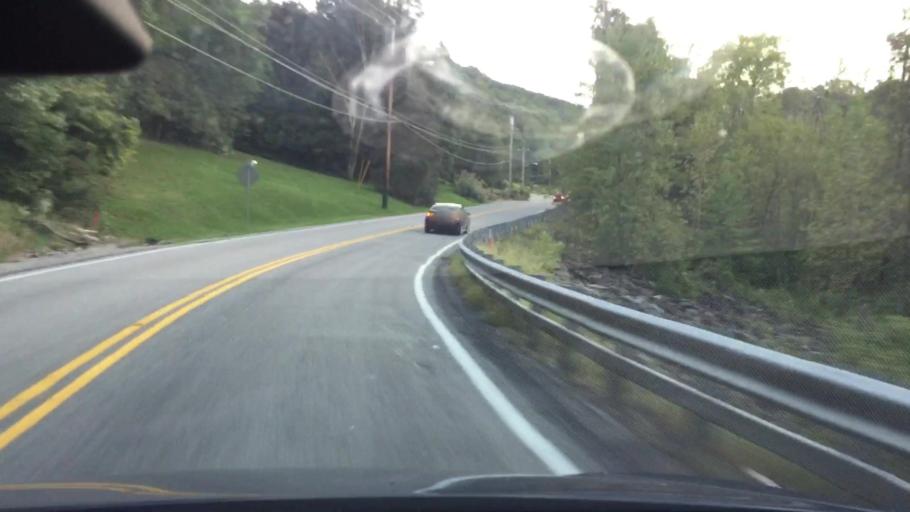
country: US
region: Pennsylvania
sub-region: Allegheny County
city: Allison Park
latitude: 40.5417
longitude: -79.9194
